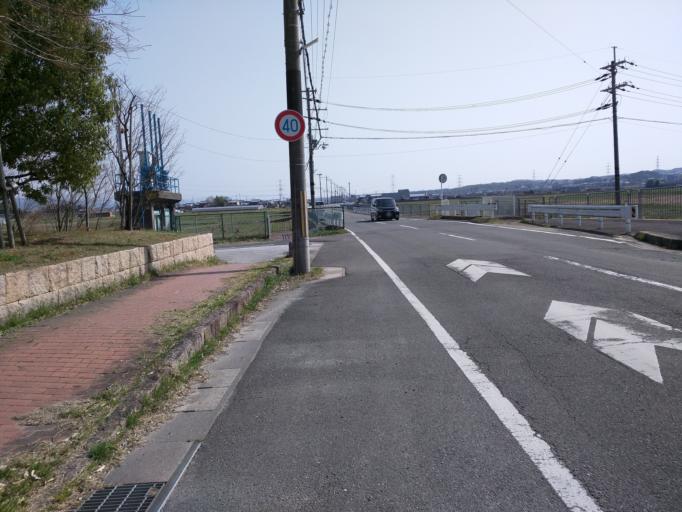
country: JP
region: Kyoto
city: Tanabe
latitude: 34.7726
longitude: 135.7975
